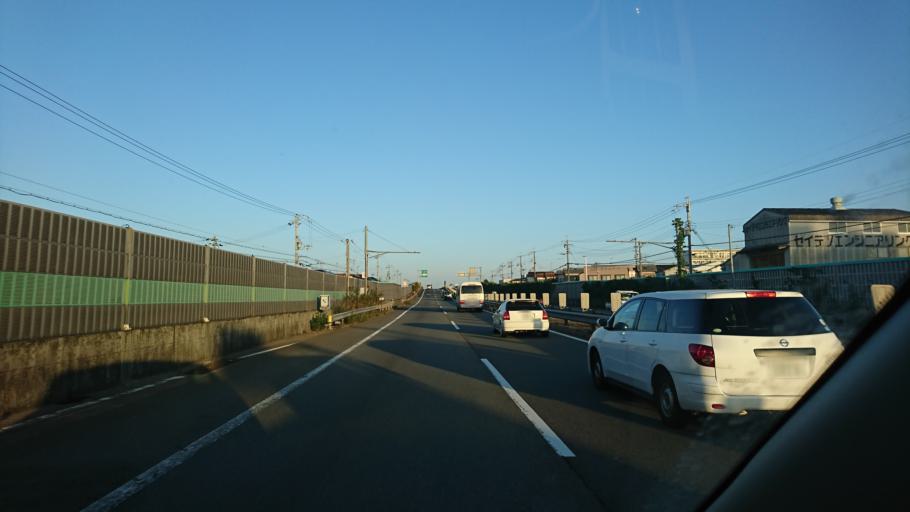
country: JP
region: Hyogo
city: Kakogawacho-honmachi
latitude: 34.7283
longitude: 134.8902
